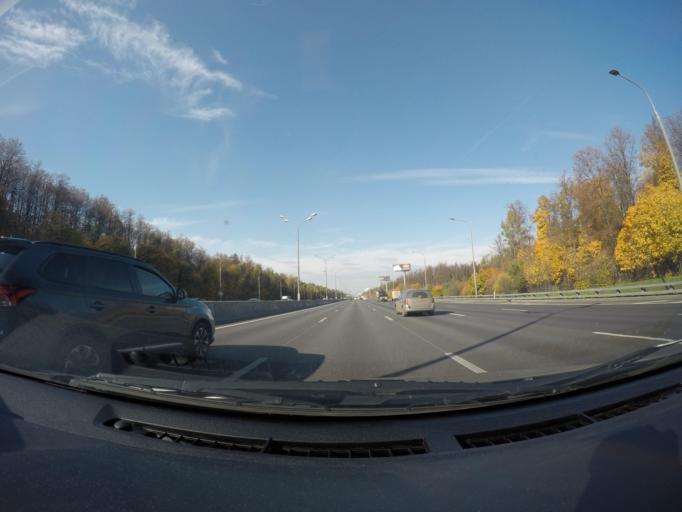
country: RU
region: Moscow
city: Gol'yanovo
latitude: 55.8397
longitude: 37.8092
